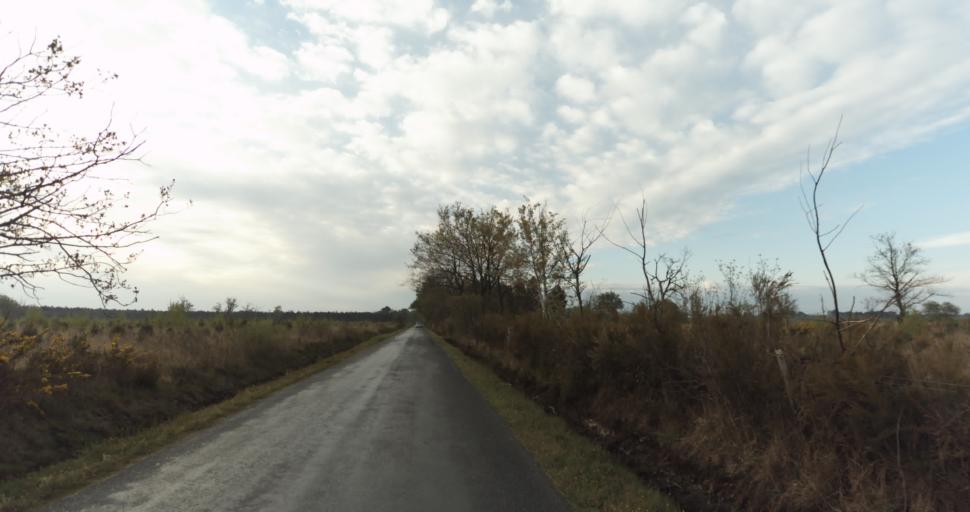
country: FR
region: Aquitaine
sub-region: Departement de la Gironde
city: Saint-Aubin-de-Medoc
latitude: 44.7804
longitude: -0.7459
